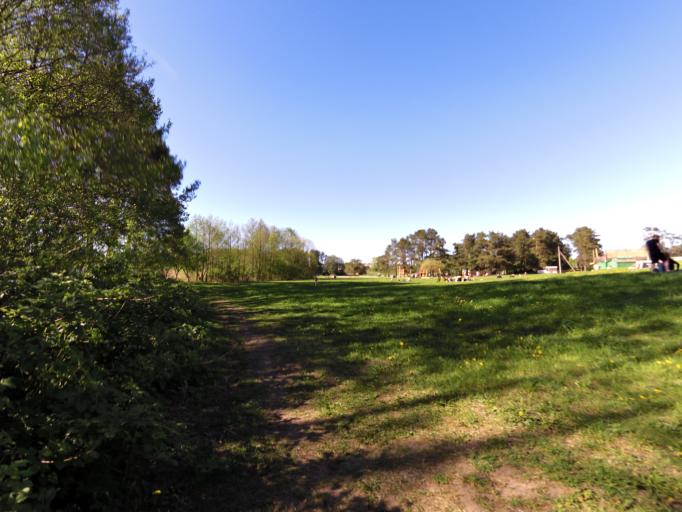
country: LT
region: Vilnius County
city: Pilaite
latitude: 54.6944
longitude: 25.1787
